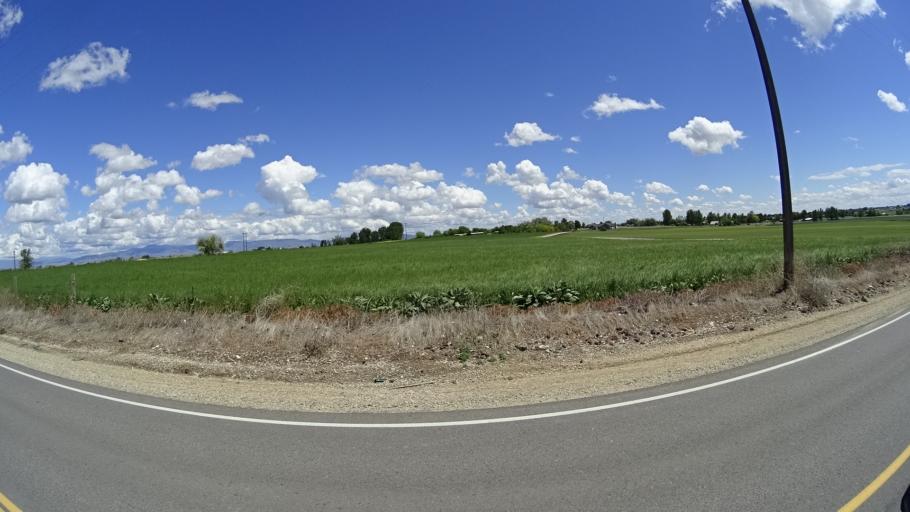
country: US
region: Idaho
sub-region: Ada County
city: Meridian
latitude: 43.5673
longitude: -116.4537
